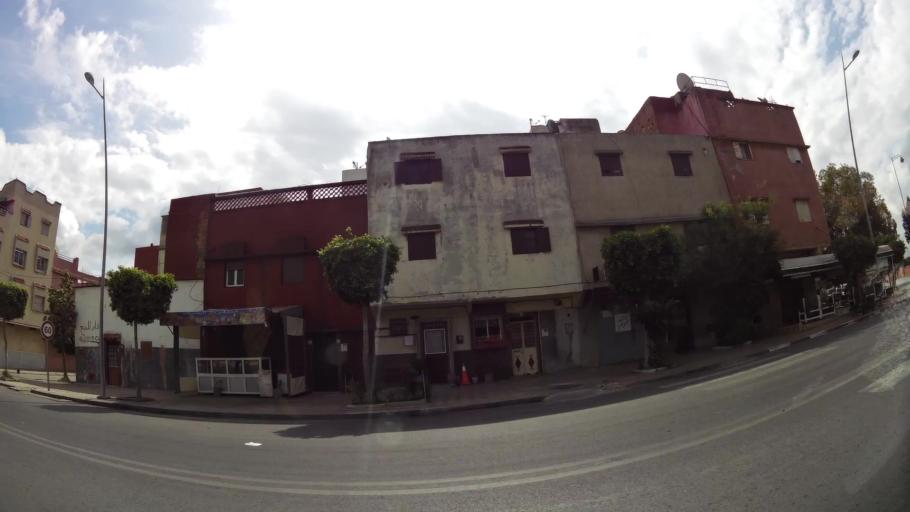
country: MA
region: Gharb-Chrarda-Beni Hssen
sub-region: Kenitra Province
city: Kenitra
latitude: 34.2558
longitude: -6.5608
